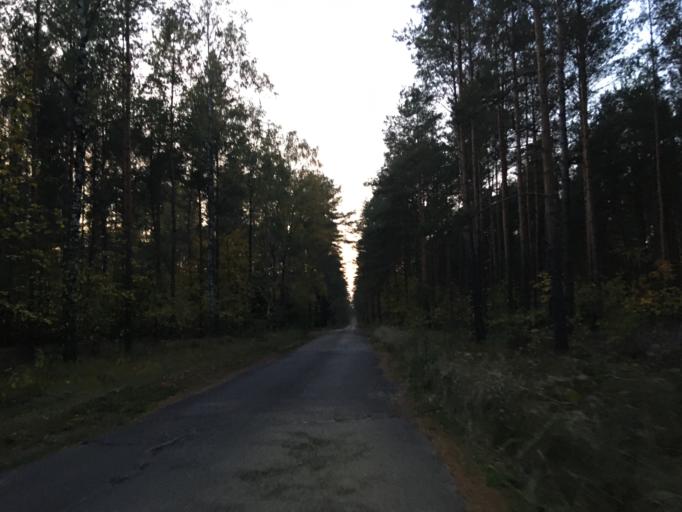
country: DE
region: Brandenburg
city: Birkenwerder
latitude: 52.6827
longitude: 13.3286
